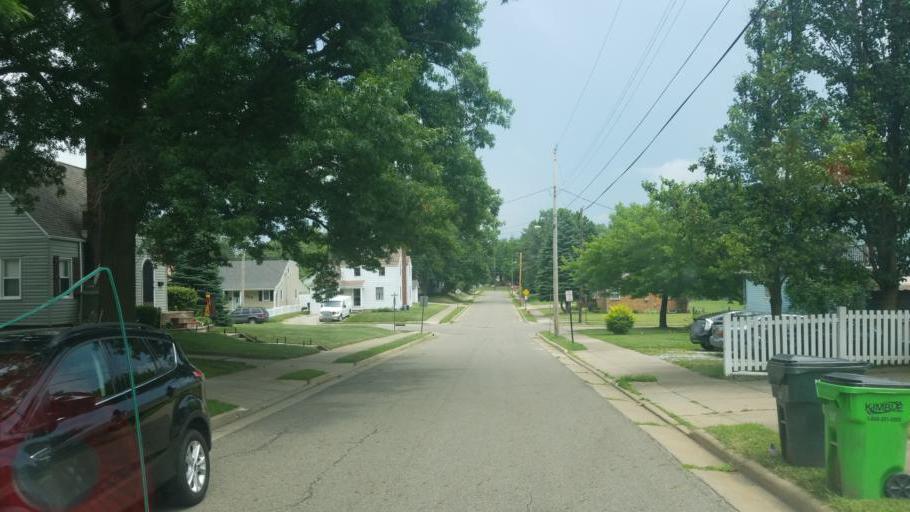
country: US
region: Ohio
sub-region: Stark County
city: North Canton
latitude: 40.8783
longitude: -81.3958
